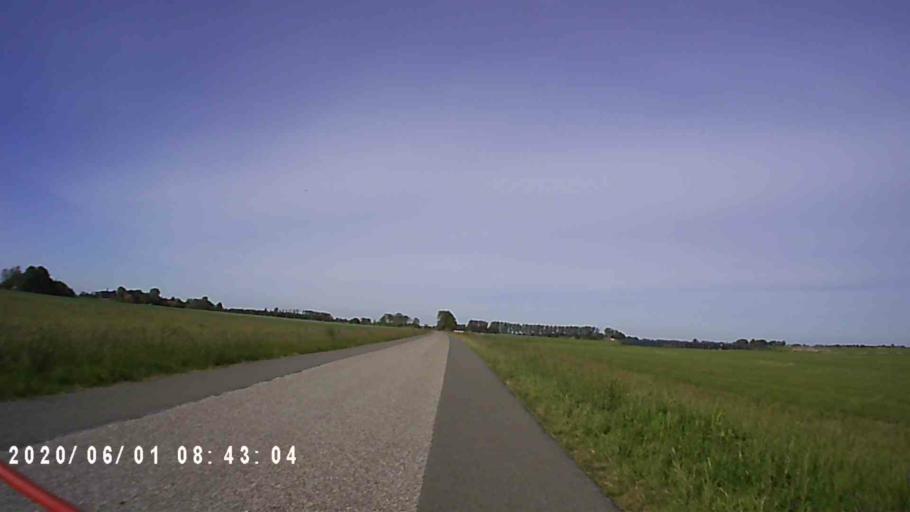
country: NL
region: Friesland
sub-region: Gemeente Ferwerderadiel
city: Burdaard
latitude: 53.2844
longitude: 5.8439
